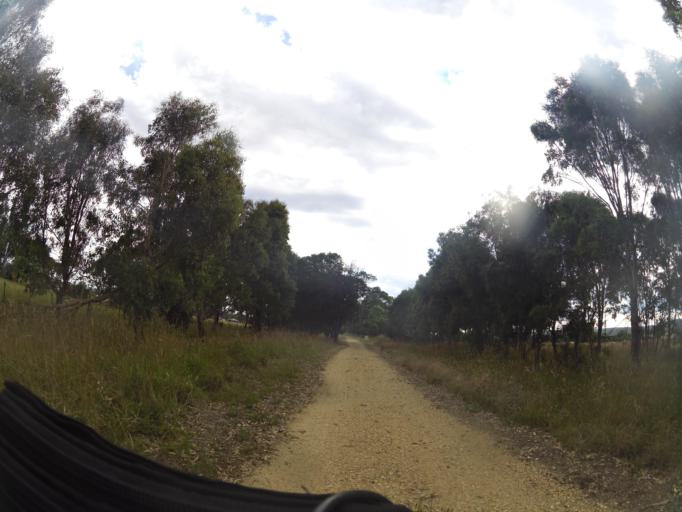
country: AU
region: Victoria
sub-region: Wellington
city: Heyfield
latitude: -38.0496
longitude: 146.6322
